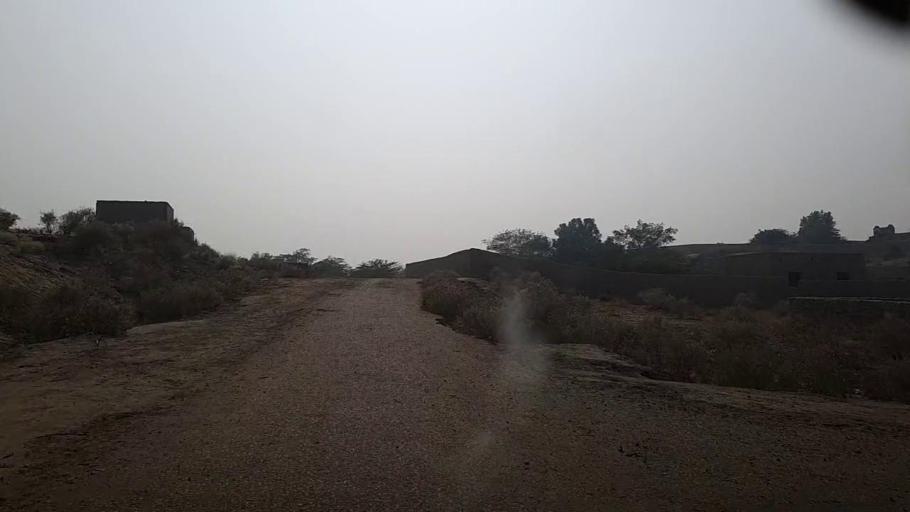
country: PK
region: Sindh
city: Bozdar
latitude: 27.0684
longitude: 68.6322
